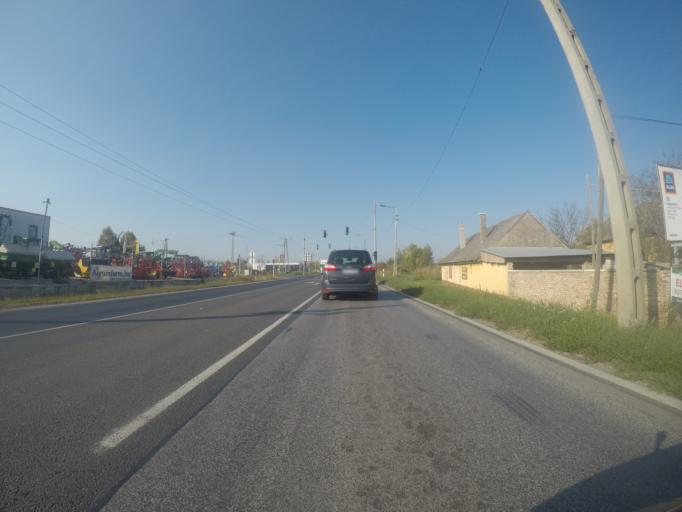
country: HU
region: Tolna
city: Dunafoldvar
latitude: 46.8085
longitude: 18.9128
